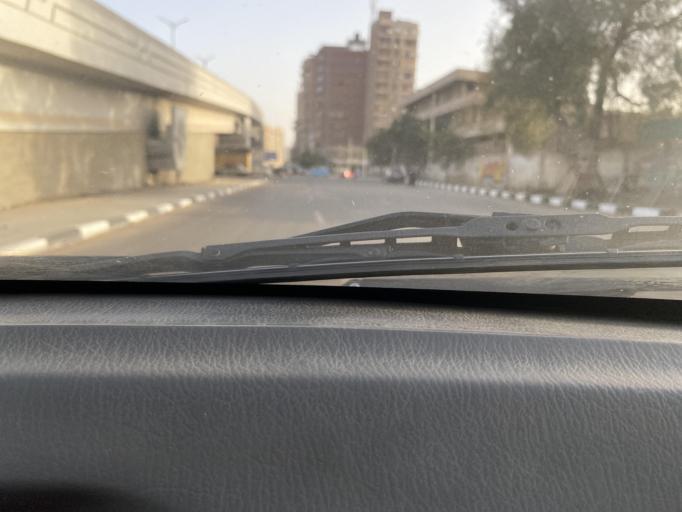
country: EG
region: Muhafazat al Qahirah
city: Cairo
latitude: 30.1150
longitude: 31.2959
